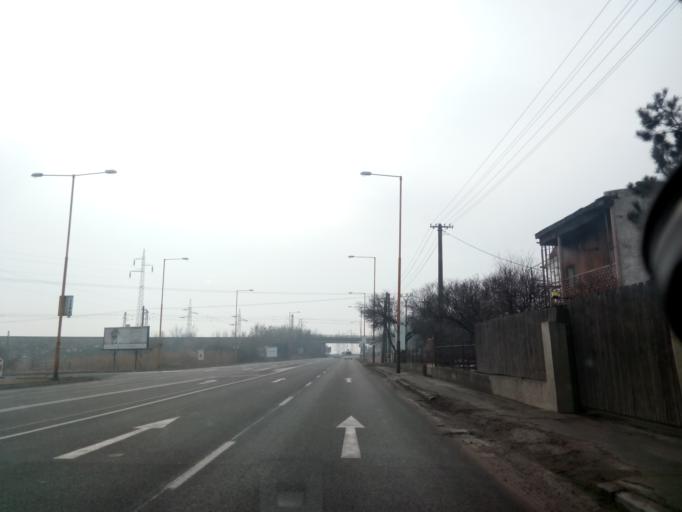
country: SK
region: Kosicky
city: Kosice
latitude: 48.6690
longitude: 21.2714
